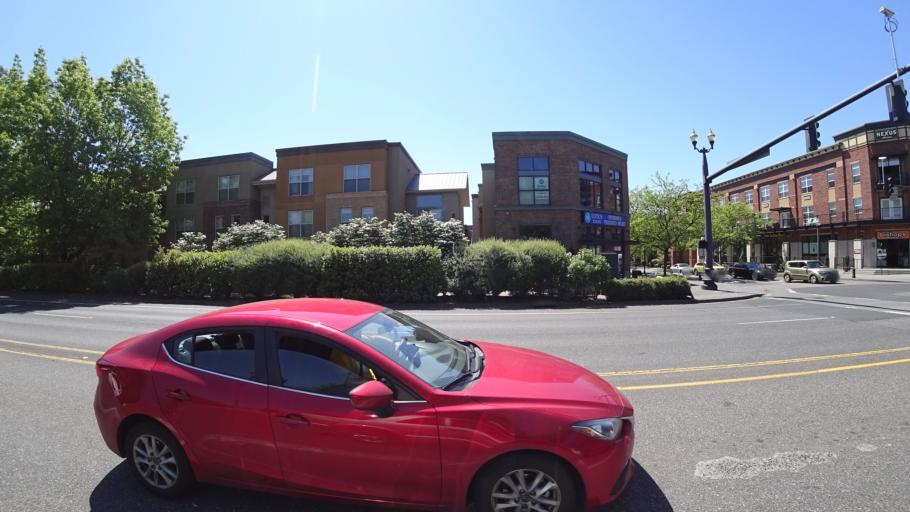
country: US
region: Oregon
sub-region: Washington County
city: Rockcreek
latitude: 45.5341
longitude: -122.9165
